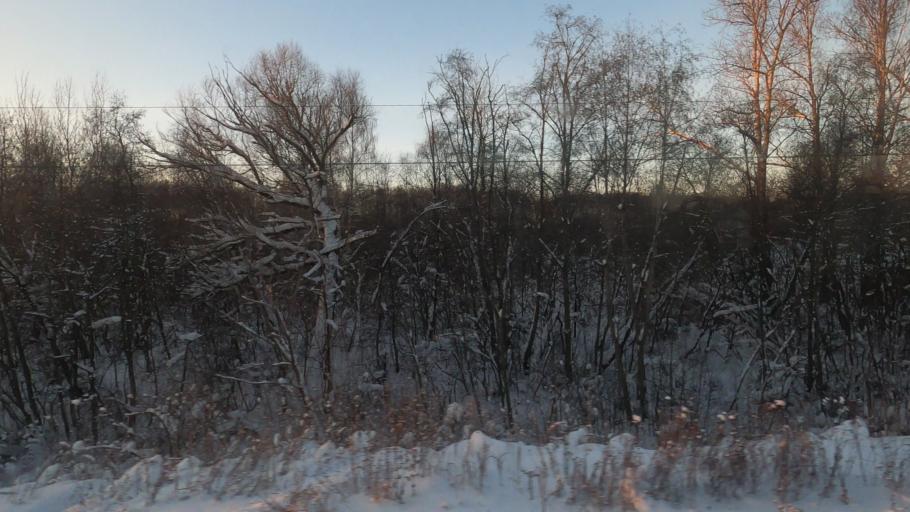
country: RU
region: Moskovskaya
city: Dmitrov
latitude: 56.3319
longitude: 37.5051
